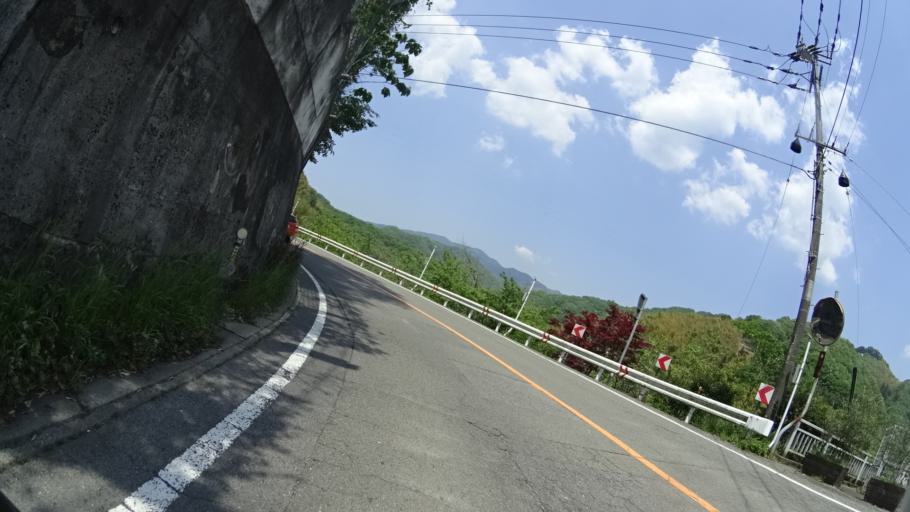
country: JP
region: Ehime
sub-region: Shikoku-chuo Shi
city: Matsuyama
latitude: 33.8807
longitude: 132.8377
